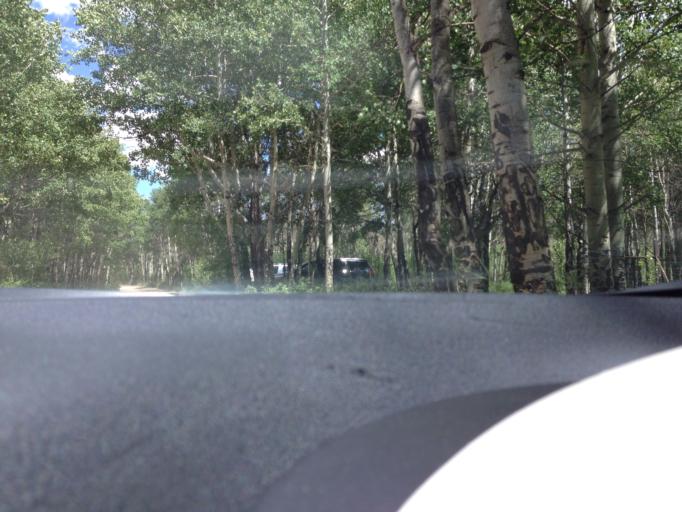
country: US
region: Colorado
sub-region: Larimer County
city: Estes Park
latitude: 40.3560
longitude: -105.6261
